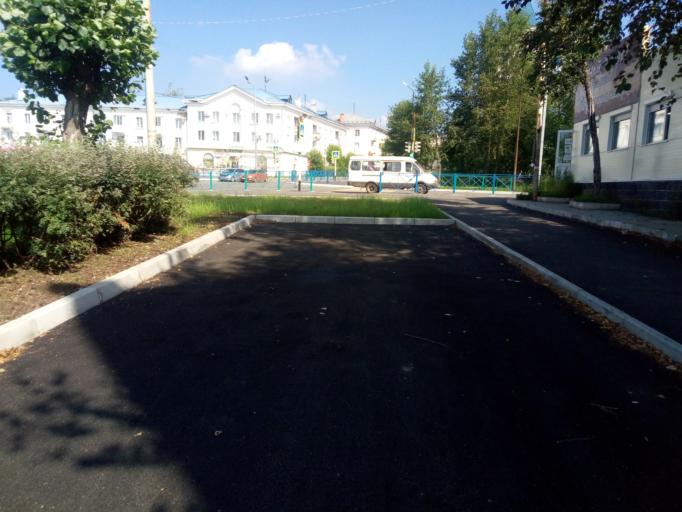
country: RU
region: Sverdlovsk
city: Krasnotur'insk
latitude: 59.7632
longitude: 60.2010
